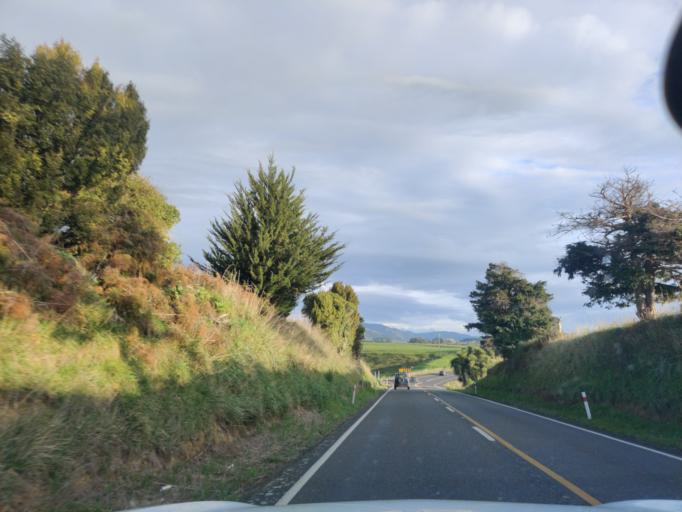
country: NZ
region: Manawatu-Wanganui
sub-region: Horowhenua District
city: Foxton
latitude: -40.5065
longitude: 175.4855
